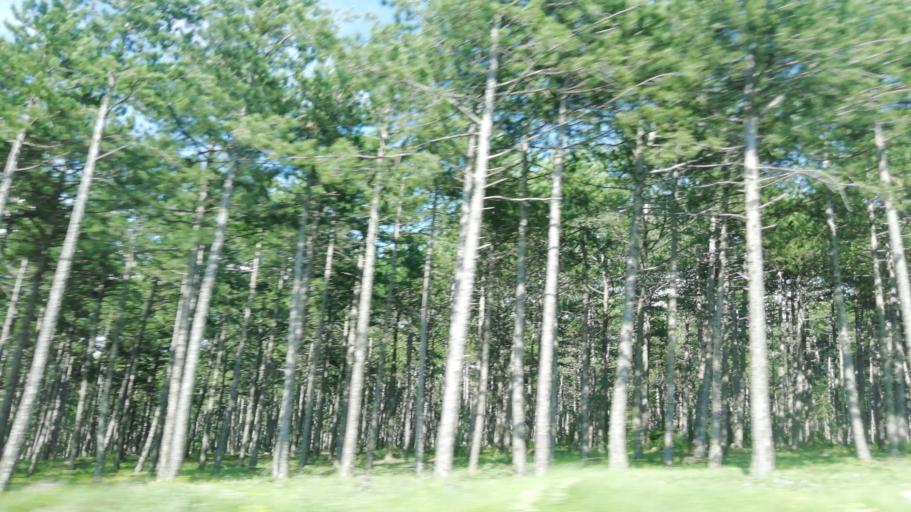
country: TR
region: Karabuk
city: Karabuk
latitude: 41.1158
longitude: 32.6053
